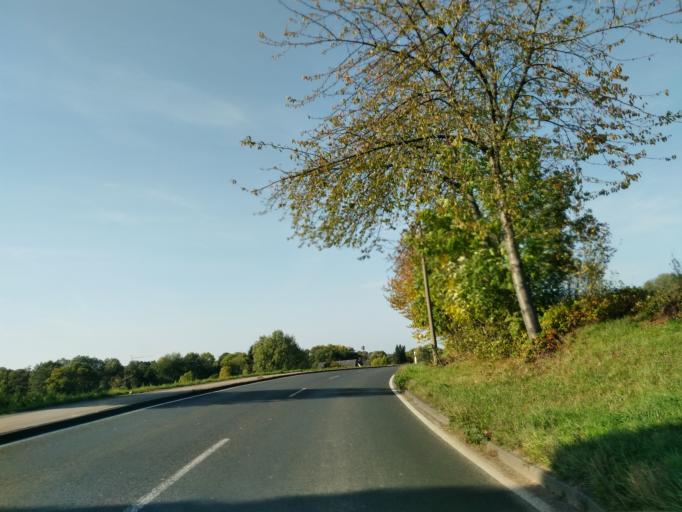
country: DE
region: North Rhine-Westphalia
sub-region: Regierungsbezirk Koln
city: Stossdorf
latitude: 50.7346
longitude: 7.2567
